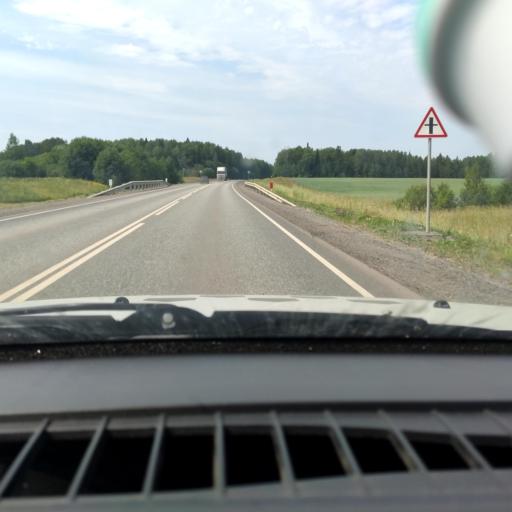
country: RU
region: Perm
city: Siva
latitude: 58.4931
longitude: 54.0522
